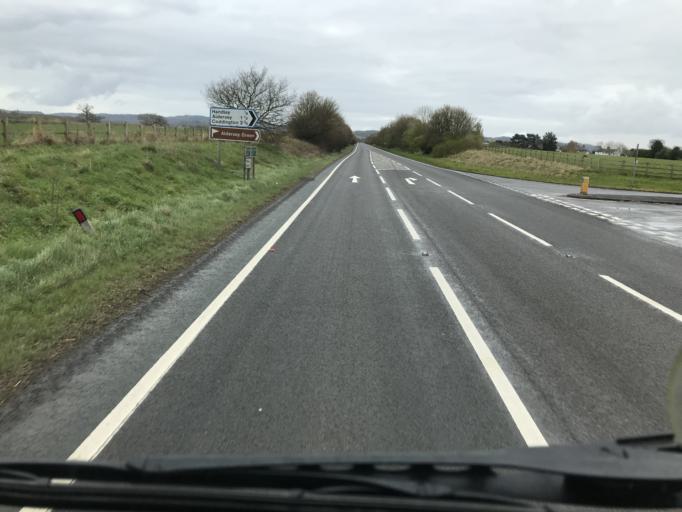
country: GB
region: England
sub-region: Cheshire West and Chester
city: Tattenhall
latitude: 53.1180
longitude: -2.7991
